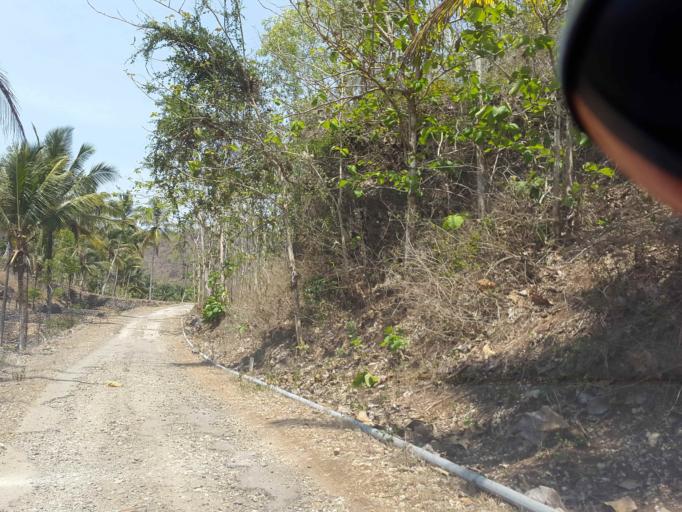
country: ID
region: East Java
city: Krajan
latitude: -8.1740
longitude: 110.9102
